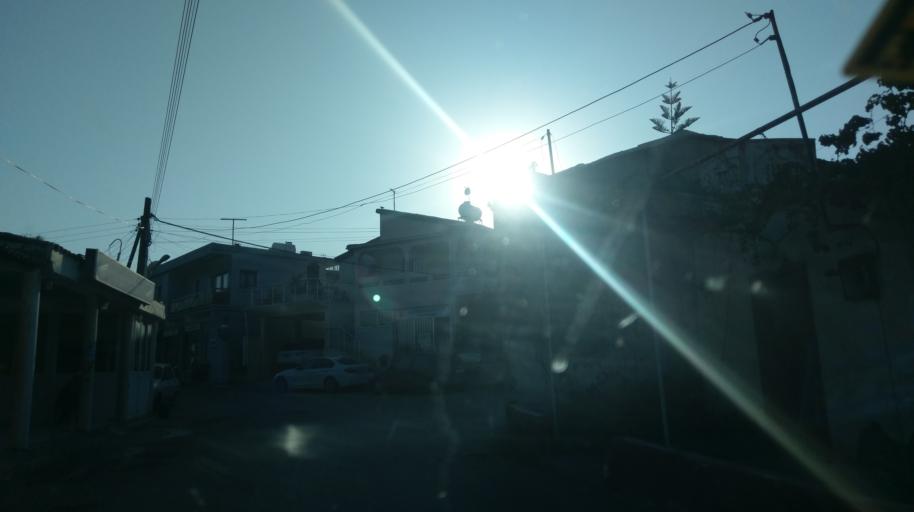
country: CY
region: Lefkosia
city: Lefka
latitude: 35.1331
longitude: 32.9126
